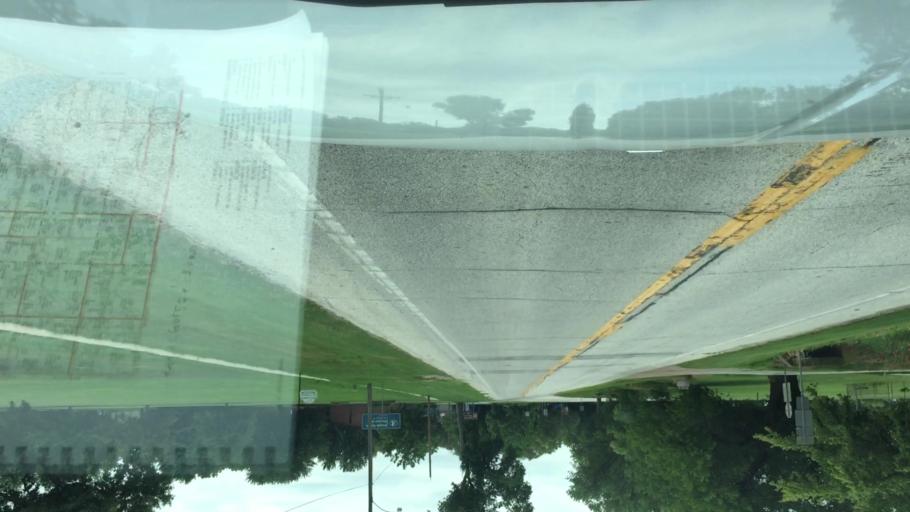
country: US
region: Illinois
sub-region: Hancock County
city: Nauvoo
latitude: 40.5423
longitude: -91.3867
